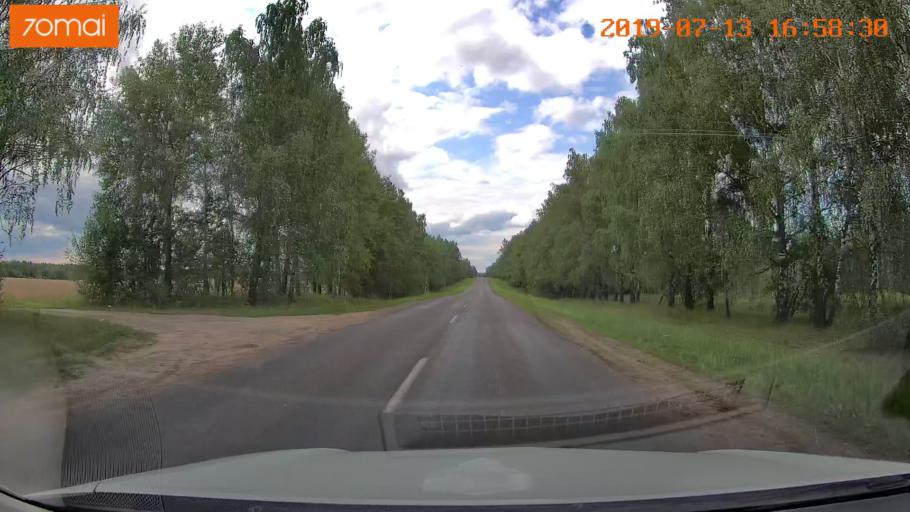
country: BY
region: Mogilev
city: Kirawsk
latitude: 53.2890
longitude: 29.4416
